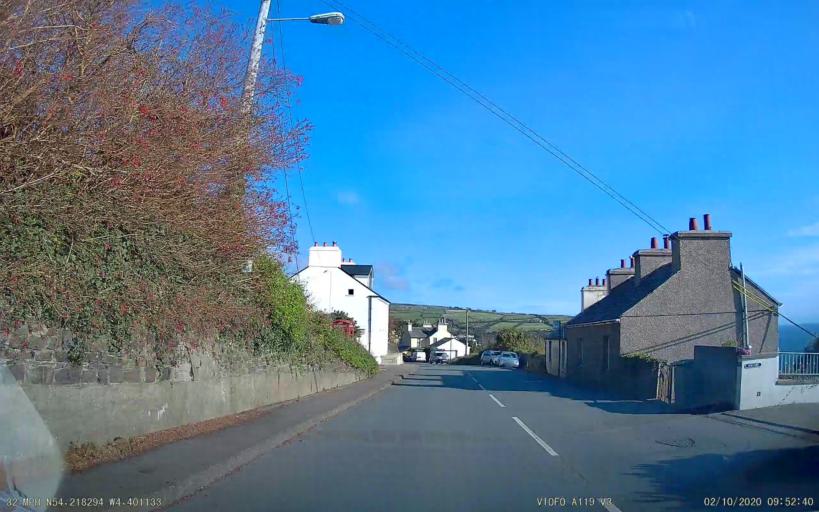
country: IM
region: Laxey
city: Laxey
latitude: 54.2184
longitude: -4.4011
